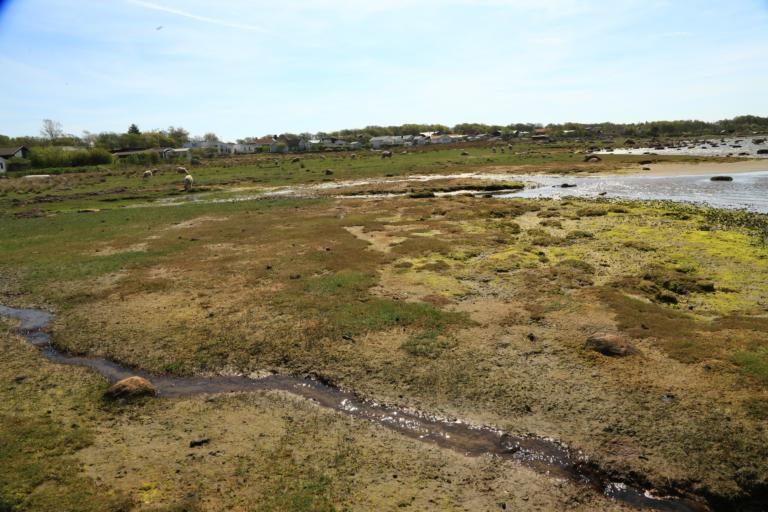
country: SE
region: Halland
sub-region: Varbergs Kommun
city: Varberg
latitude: 57.1401
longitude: 12.2186
